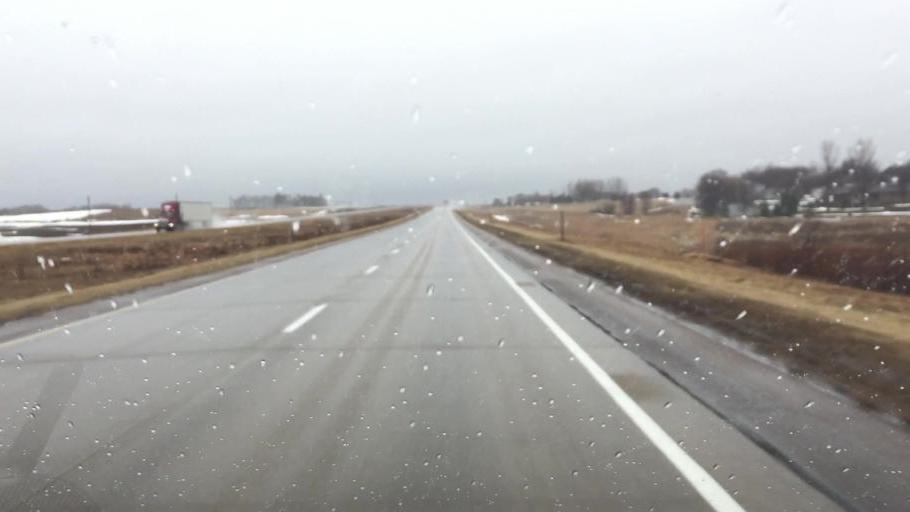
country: US
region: Iowa
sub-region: O'Brien County
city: Sheldon
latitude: 43.0790
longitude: -95.8998
